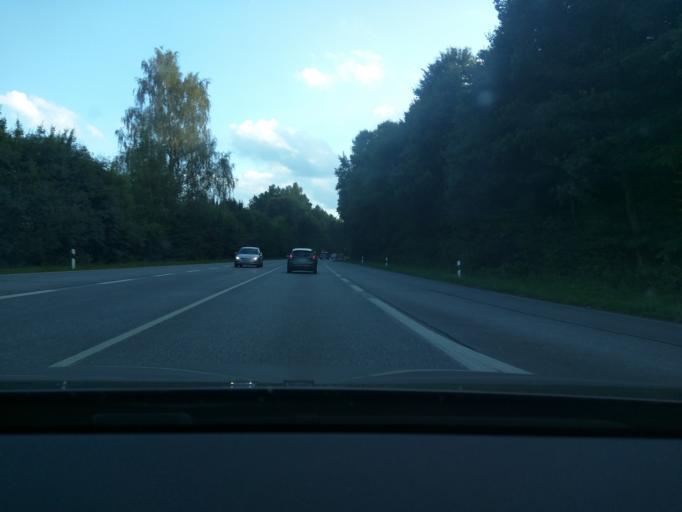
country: DE
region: Schleswig-Holstein
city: Gronwohld
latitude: 53.6338
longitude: 10.3906
